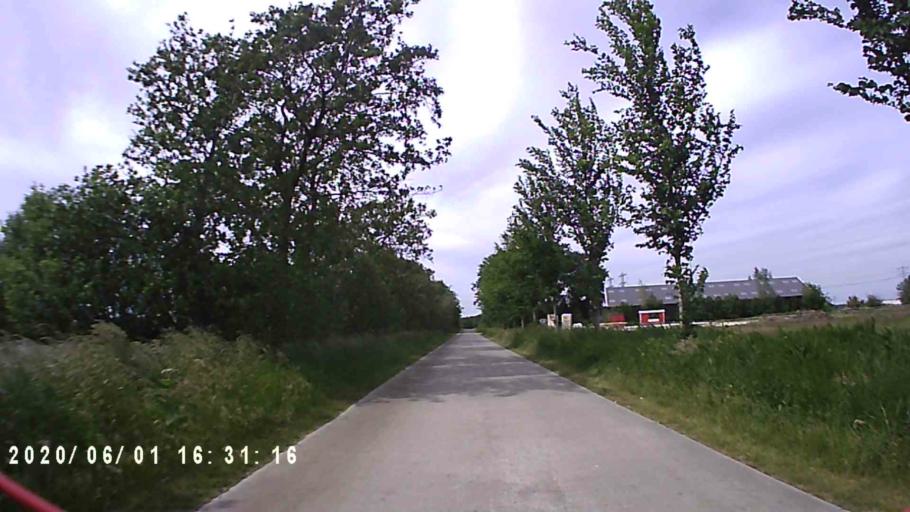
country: NL
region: Friesland
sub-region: Gemeente Leeuwarden
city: Camminghaburen
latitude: 53.1861
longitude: 5.8663
